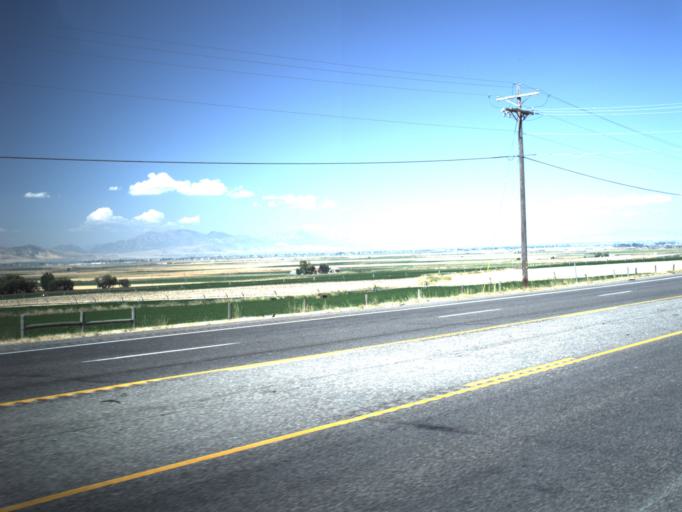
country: US
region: Utah
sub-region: Cache County
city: Smithfield
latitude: 41.8673
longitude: -111.8286
